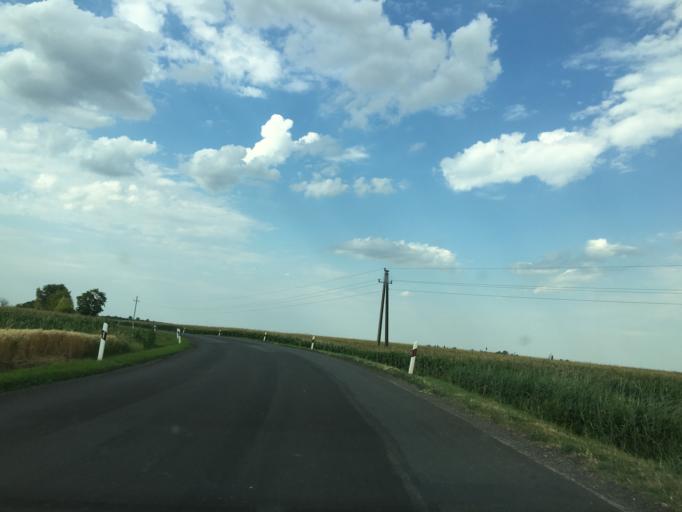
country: HU
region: Bacs-Kiskun
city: Dusnok
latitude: 46.4251
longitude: 18.9443
